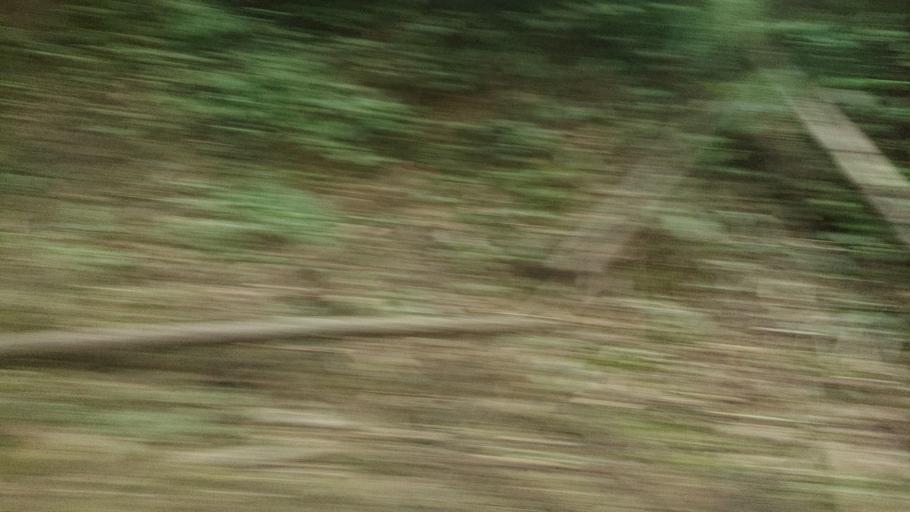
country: TW
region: Taiwan
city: Lugu
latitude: 23.6240
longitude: 120.7150
